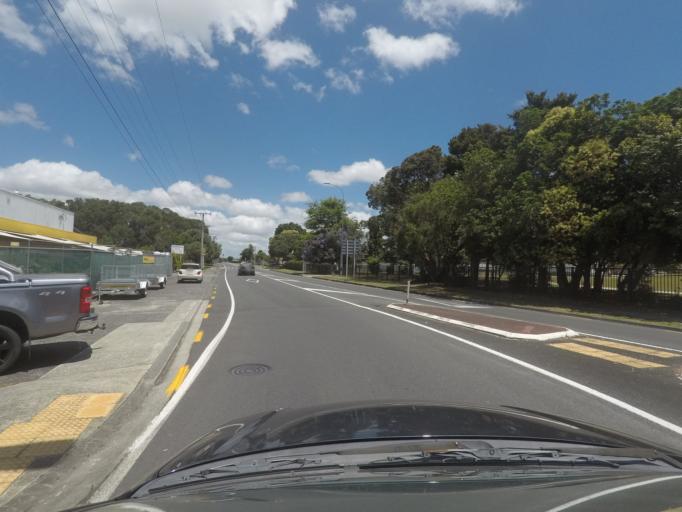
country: NZ
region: Northland
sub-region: Whangarei
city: Whangarei
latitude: -35.7573
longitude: 174.3681
